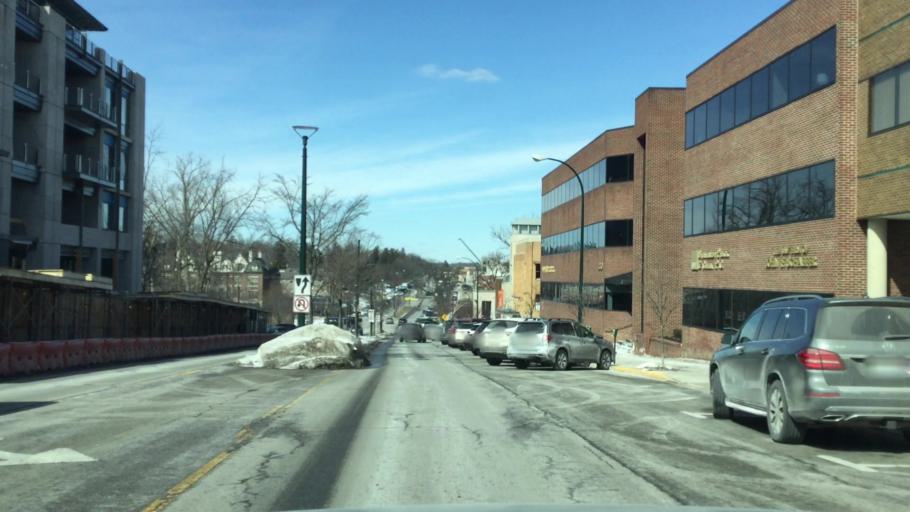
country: US
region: Michigan
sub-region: Oakland County
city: Birmingham
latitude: 42.5489
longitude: -83.2162
